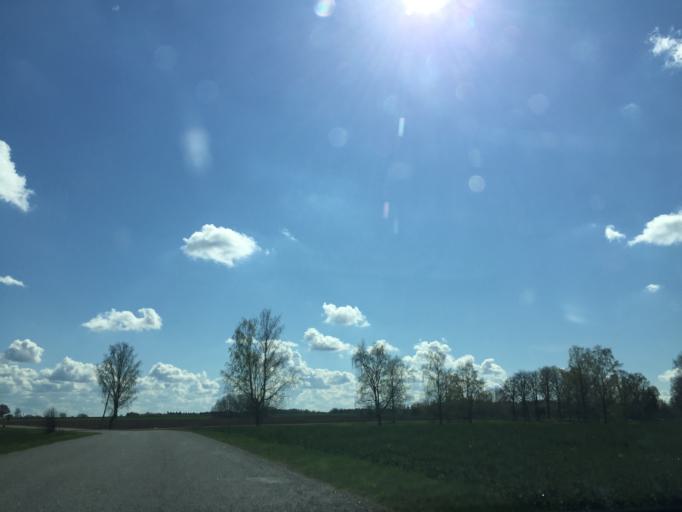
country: LV
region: Strenci
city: Strenci
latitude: 57.5247
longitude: 25.6829
